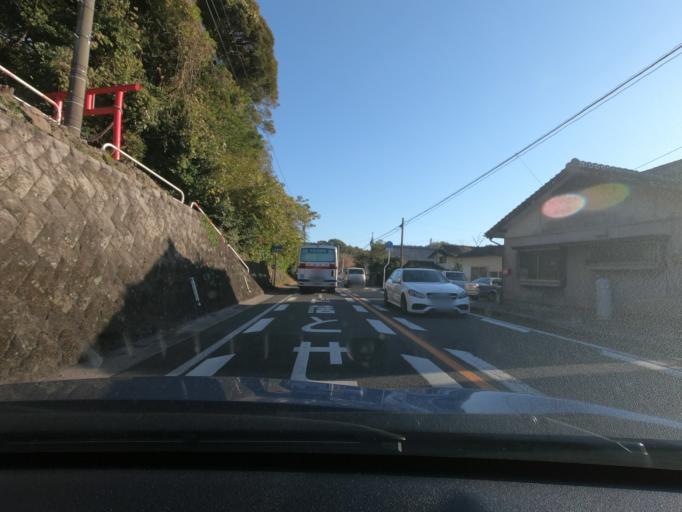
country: JP
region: Kagoshima
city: Akune
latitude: 31.9916
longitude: 130.1976
